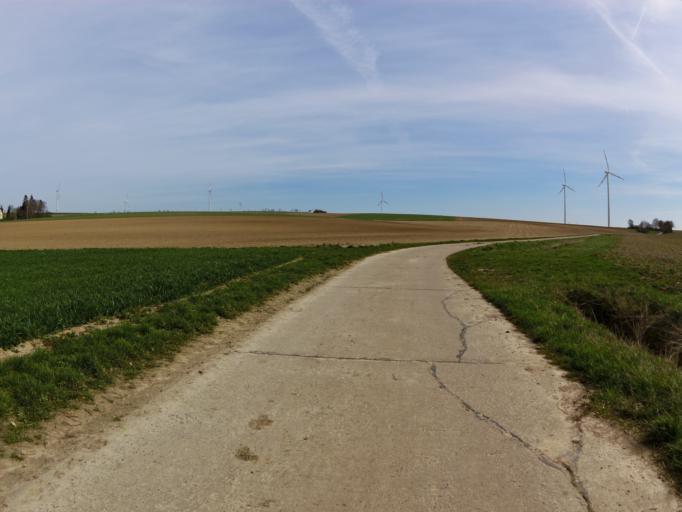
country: DE
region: Bavaria
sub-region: Regierungsbezirk Unterfranken
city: Biebelried
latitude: 49.7613
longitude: 10.0855
